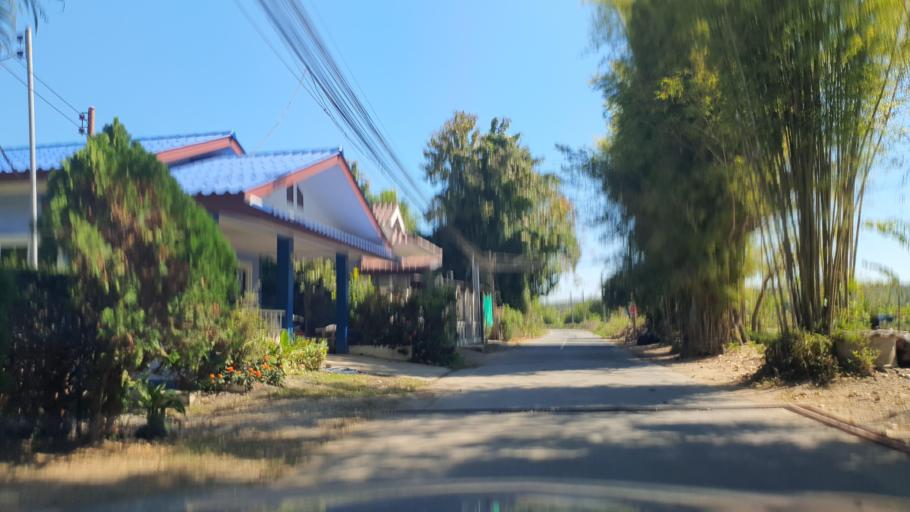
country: TH
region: Chiang Mai
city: Mae Wang
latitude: 18.6647
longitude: 98.8299
